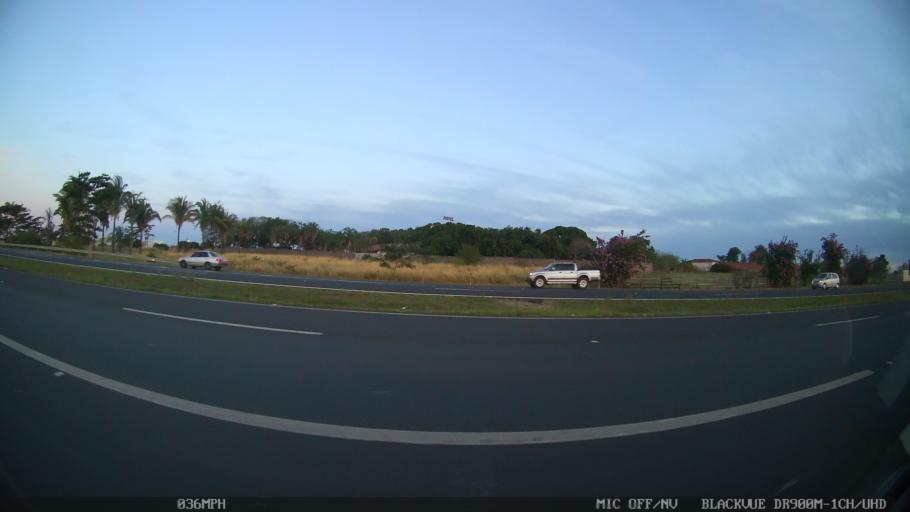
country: BR
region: Sao Paulo
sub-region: Catanduva
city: Catanduva
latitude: -21.1095
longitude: -48.9641
